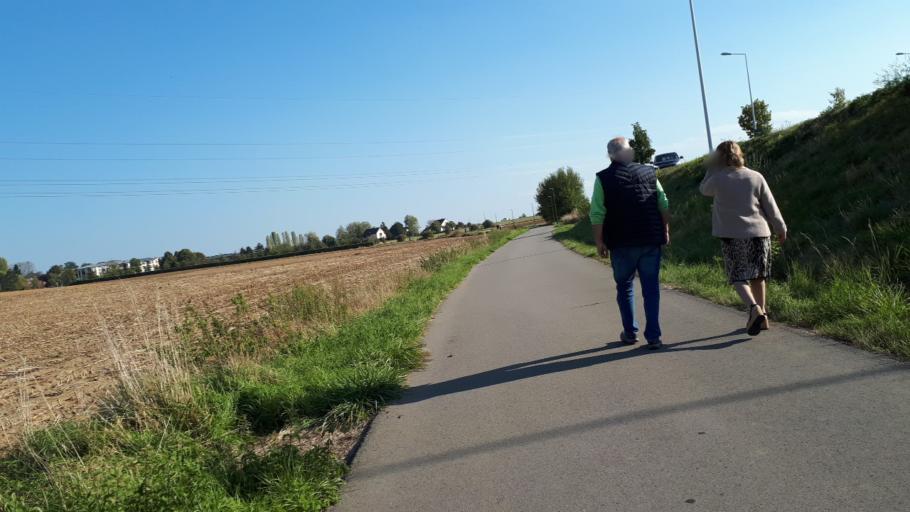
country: LU
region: Luxembourg
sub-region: Canton de Luxembourg
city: Bertrange
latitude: 49.6185
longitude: 6.0384
